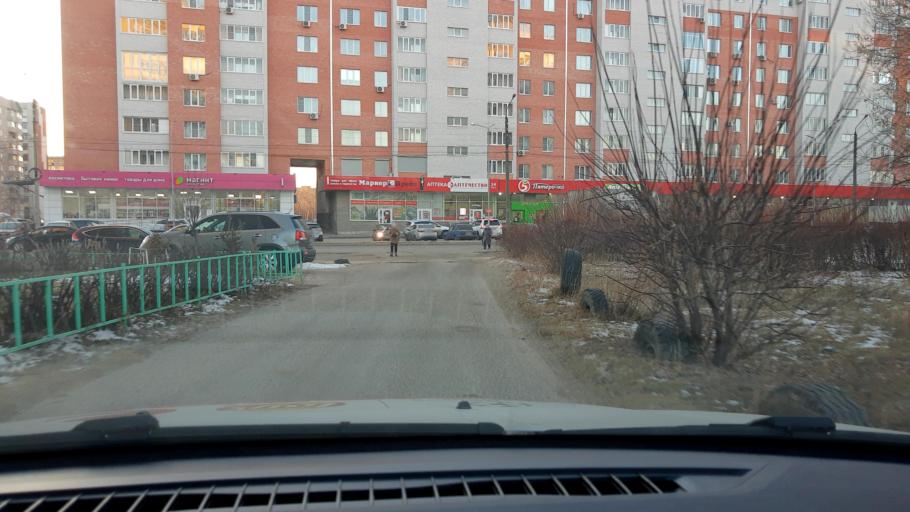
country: RU
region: Nizjnij Novgorod
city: Dzerzhinsk
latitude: 56.2325
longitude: 43.4028
